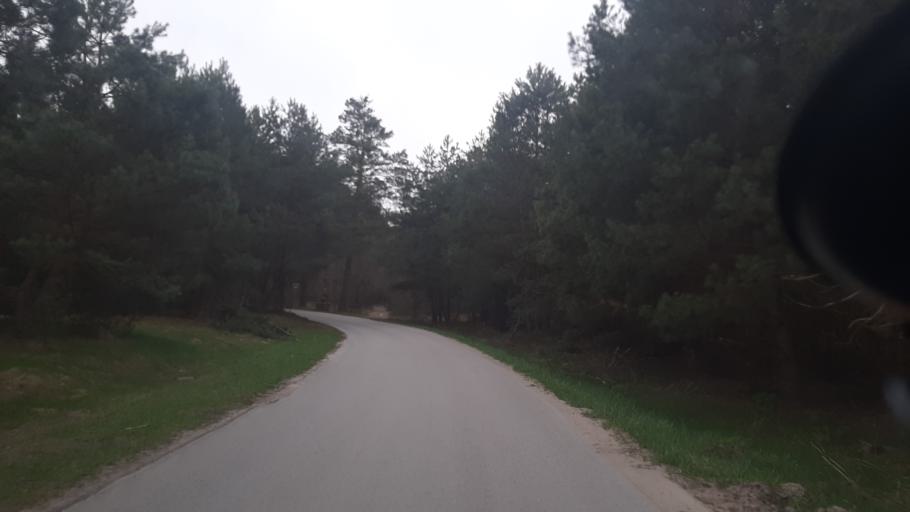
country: PL
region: Lublin Voivodeship
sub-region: Powiat lubelski
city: Niemce
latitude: 51.3811
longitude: 22.5553
